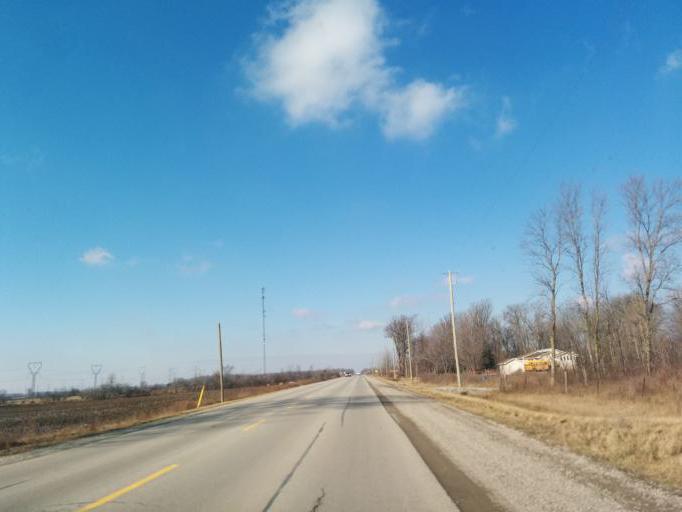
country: CA
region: Ontario
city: Brantford
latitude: 43.0060
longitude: -80.1710
